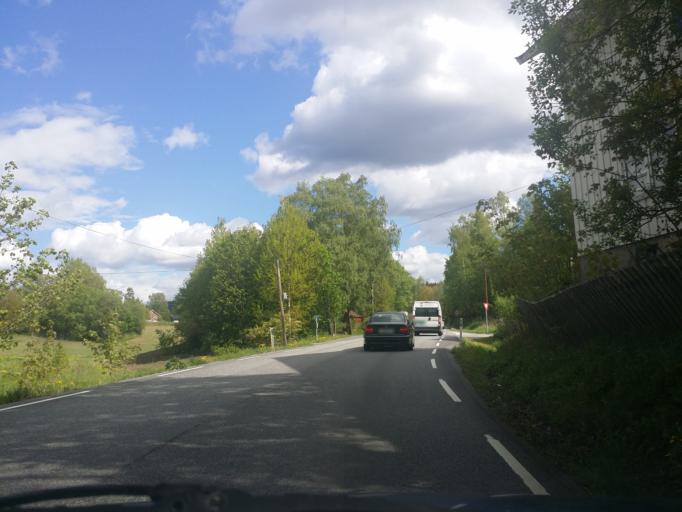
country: NO
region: Oppland
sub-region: Jevnaker
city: Jevnaker
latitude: 60.2672
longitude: 10.4830
